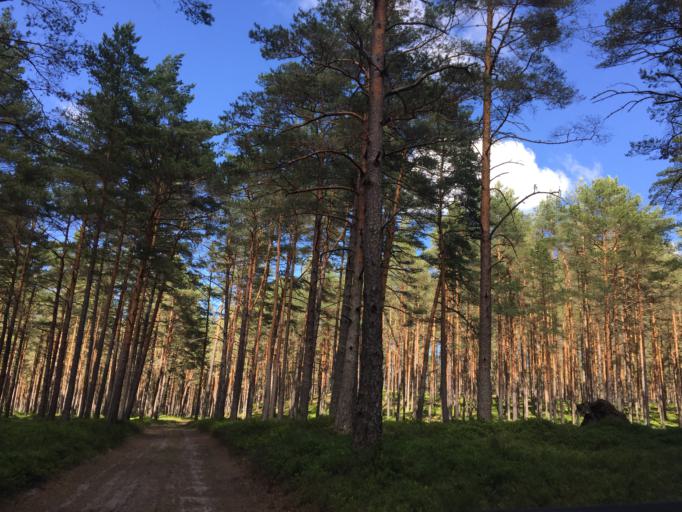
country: LV
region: Ventspils
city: Ventspils
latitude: 57.4668
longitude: 21.6384
